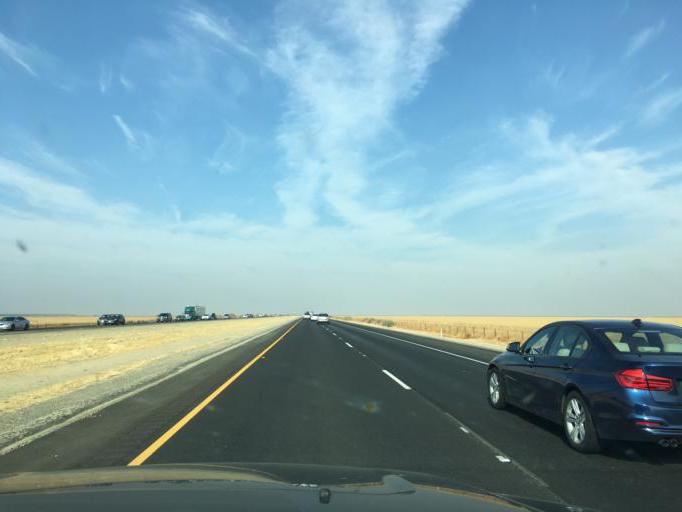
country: US
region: California
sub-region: Kern County
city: Lost Hills
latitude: 35.6458
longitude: -119.6750
